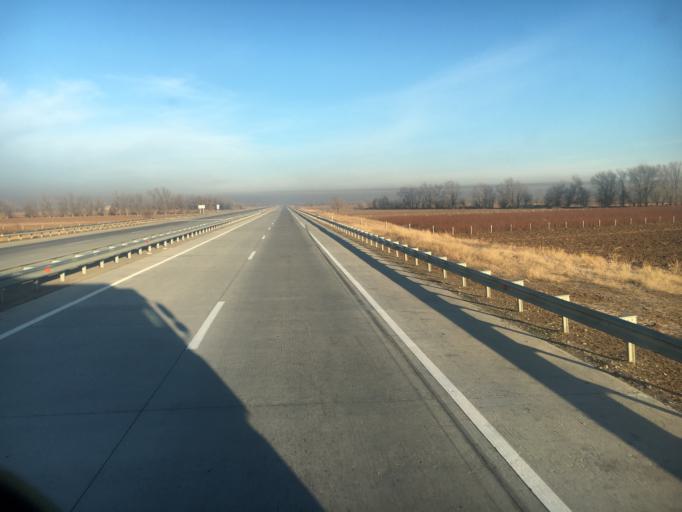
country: KZ
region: Ongtustik Qazaqstan
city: Turkestan
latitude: 43.1842
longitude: 68.4967
